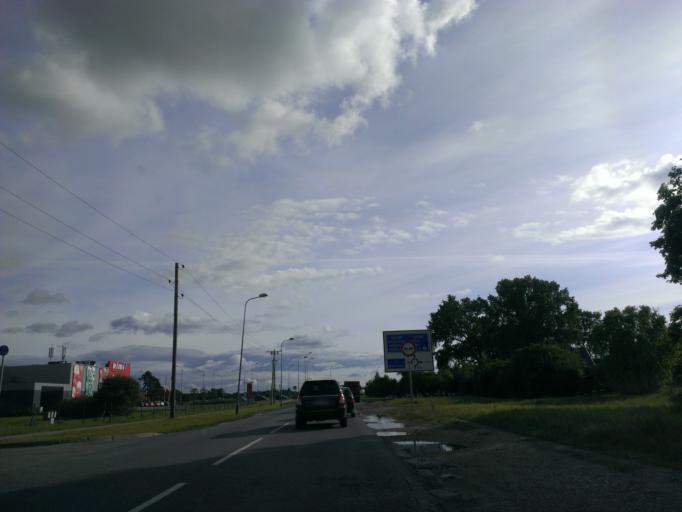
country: LV
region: Stopini
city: Ulbroka
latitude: 56.9582
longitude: 24.2527
